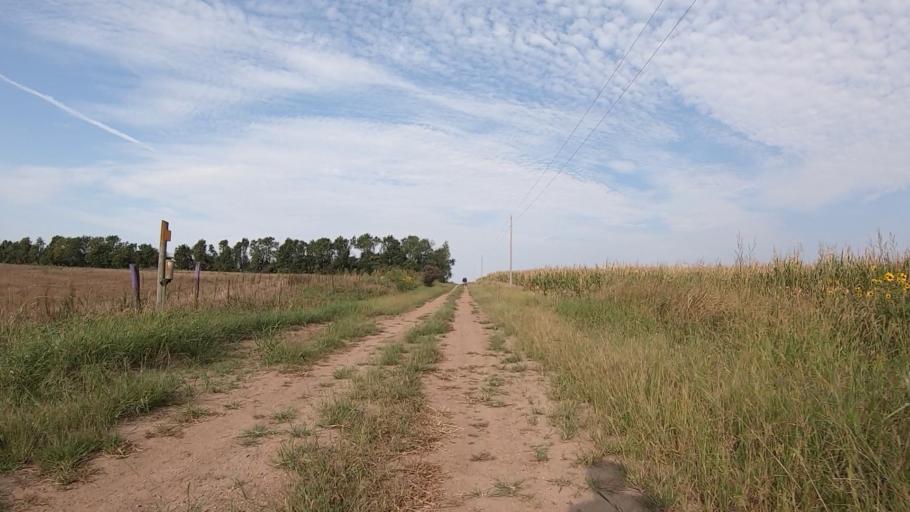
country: US
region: Kansas
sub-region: Washington County
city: Washington
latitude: 39.6750
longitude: -96.9504
